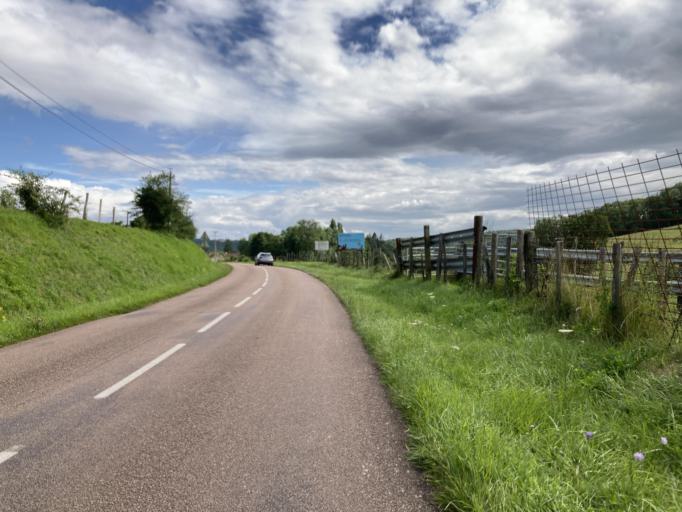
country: FR
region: Bourgogne
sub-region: Departement de la Cote-d'Or
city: Montbard
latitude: 47.6280
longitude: 4.3668
